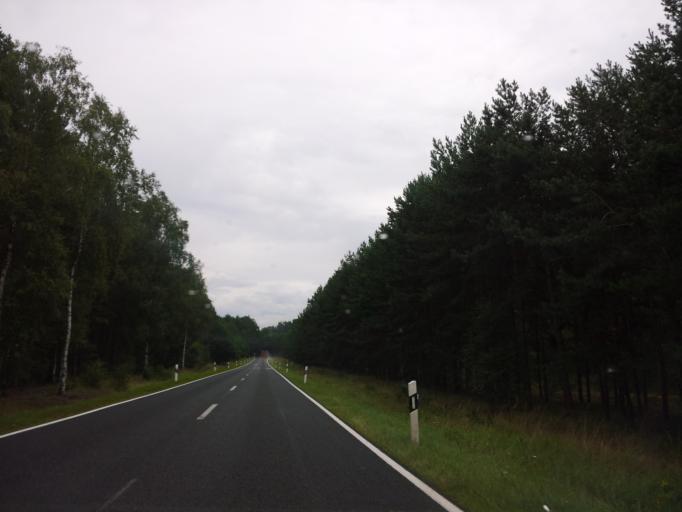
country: DE
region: Brandenburg
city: Wiesenburg
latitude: 52.1698
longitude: 12.4292
